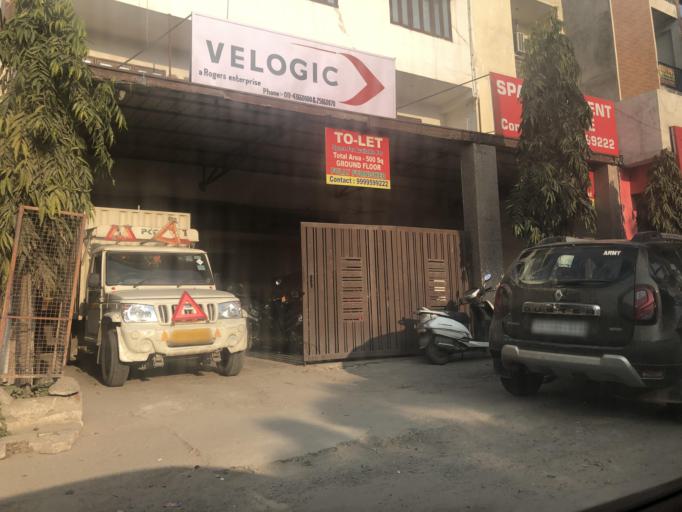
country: IN
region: Haryana
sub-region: Gurgaon
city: Gurgaon
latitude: 28.5307
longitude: 77.0863
